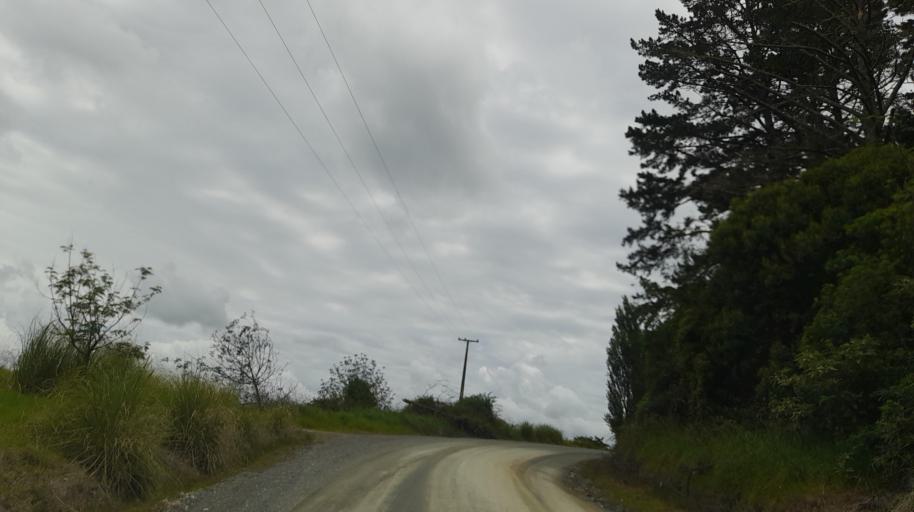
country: NZ
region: Auckland
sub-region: Auckland
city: Wellsford
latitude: -36.2457
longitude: 174.4207
